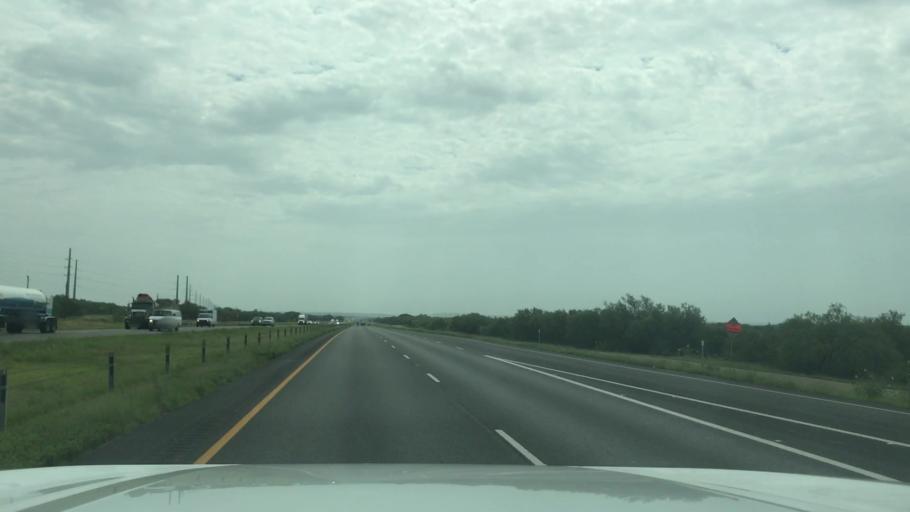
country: US
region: Texas
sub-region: Callahan County
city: Baird
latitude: 32.3910
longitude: -99.3420
